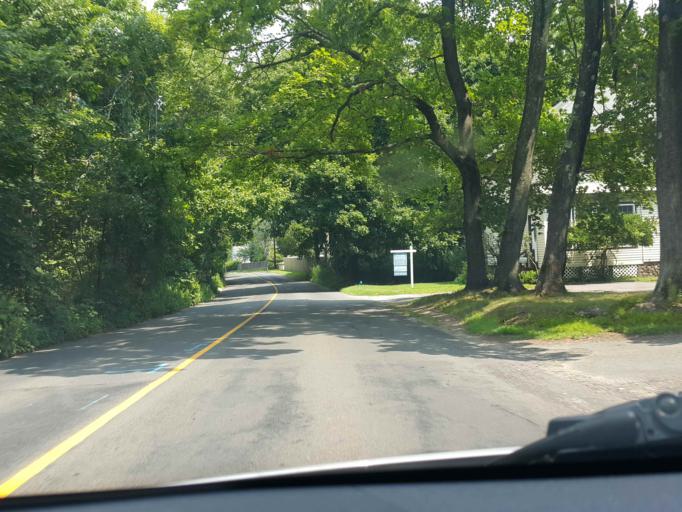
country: US
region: Connecticut
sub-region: New Haven County
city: Guilford
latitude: 41.2827
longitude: -72.6874
